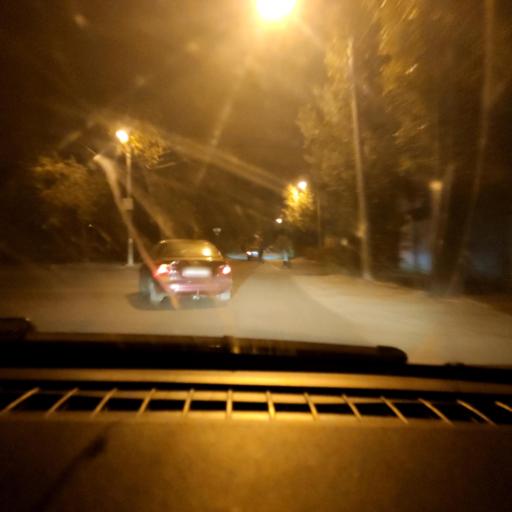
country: RU
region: Voronezj
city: Maslovka
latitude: 51.6364
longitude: 39.2730
